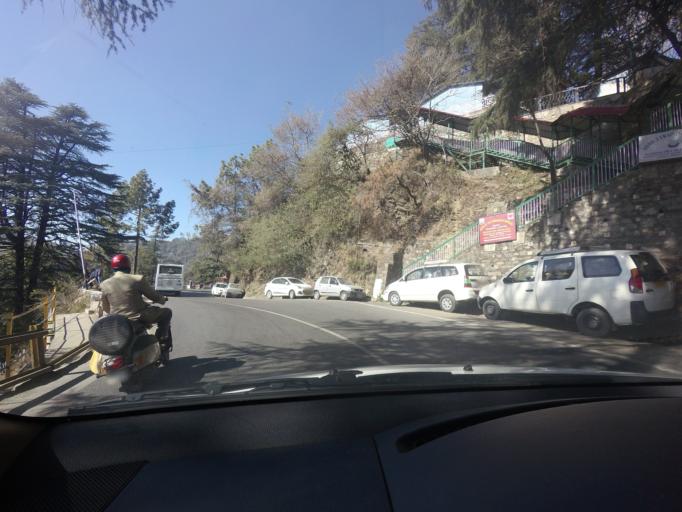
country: IN
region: Himachal Pradesh
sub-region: Shimla
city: Shimla
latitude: 31.1010
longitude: 77.1506
